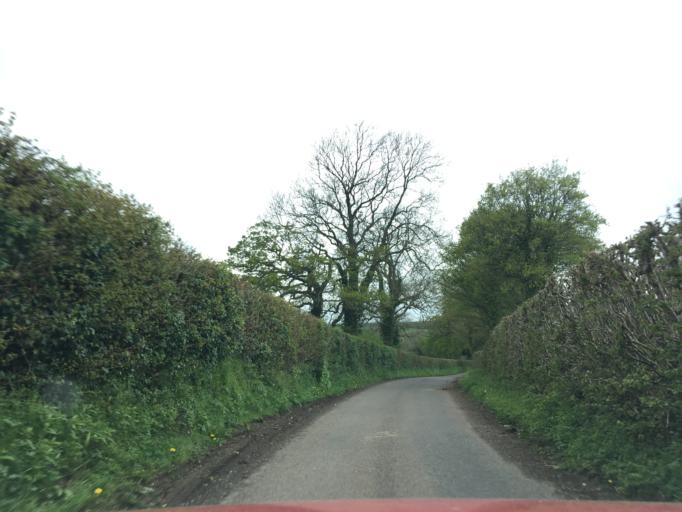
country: GB
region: England
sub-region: Bath and North East Somerset
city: Clutton
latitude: 51.3368
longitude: -2.5350
